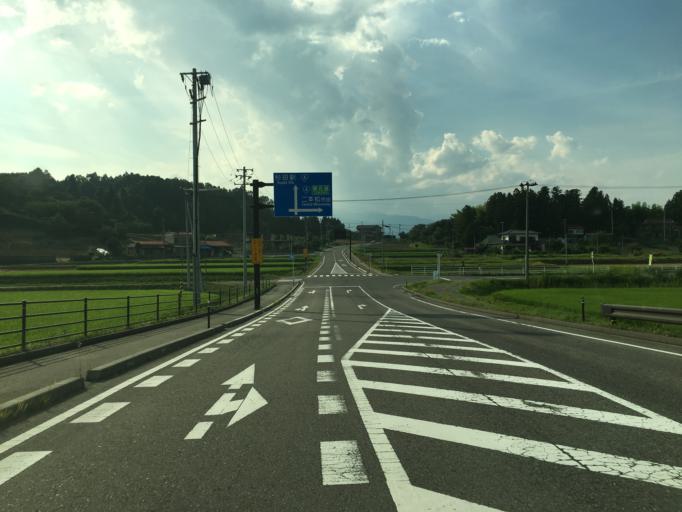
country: JP
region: Fukushima
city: Nihommatsu
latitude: 37.5546
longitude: 140.4343
